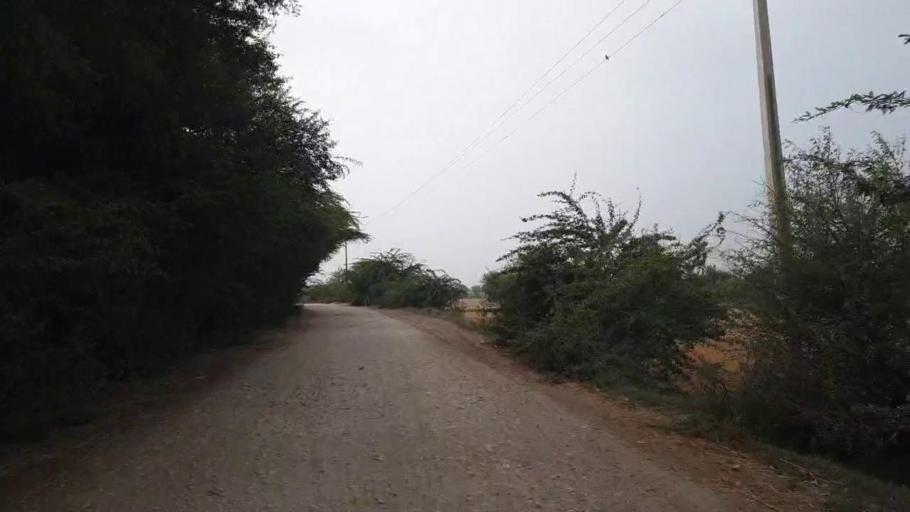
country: PK
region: Sindh
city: Matli
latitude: 24.9570
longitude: 68.5824
